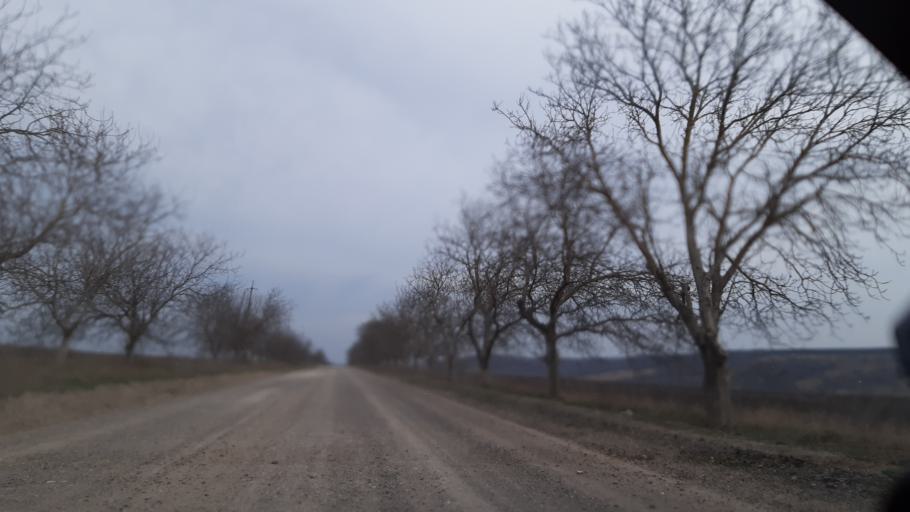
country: MD
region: Soldanesti
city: Soldanesti
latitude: 47.6950
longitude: 28.7329
